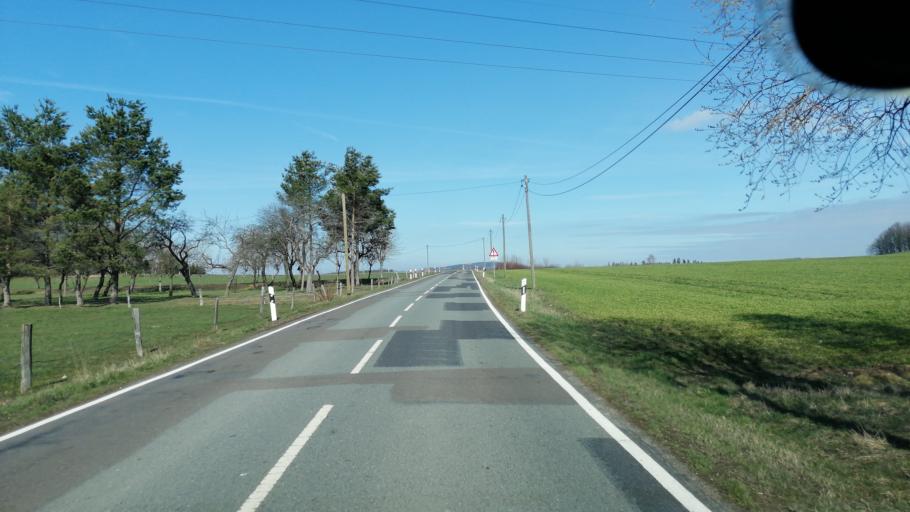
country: DE
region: Saxony
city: Schonbach
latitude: 51.0697
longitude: 14.5526
